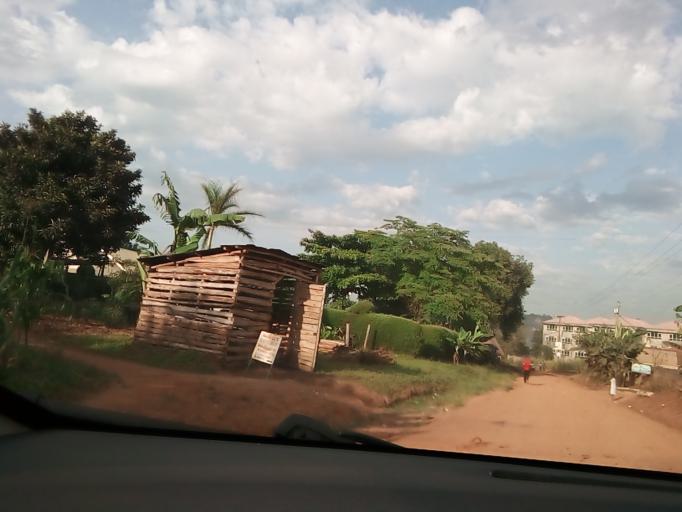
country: UG
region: Central Region
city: Masaka
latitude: -0.3444
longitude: 31.7265
